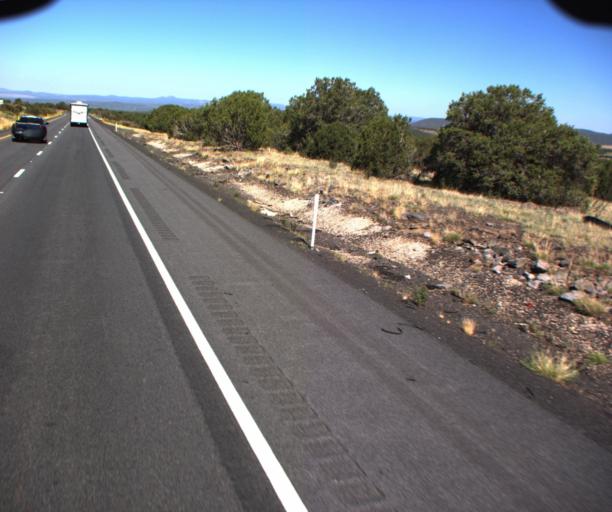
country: US
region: Arizona
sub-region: Coconino County
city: Williams
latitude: 35.2161
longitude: -112.3651
